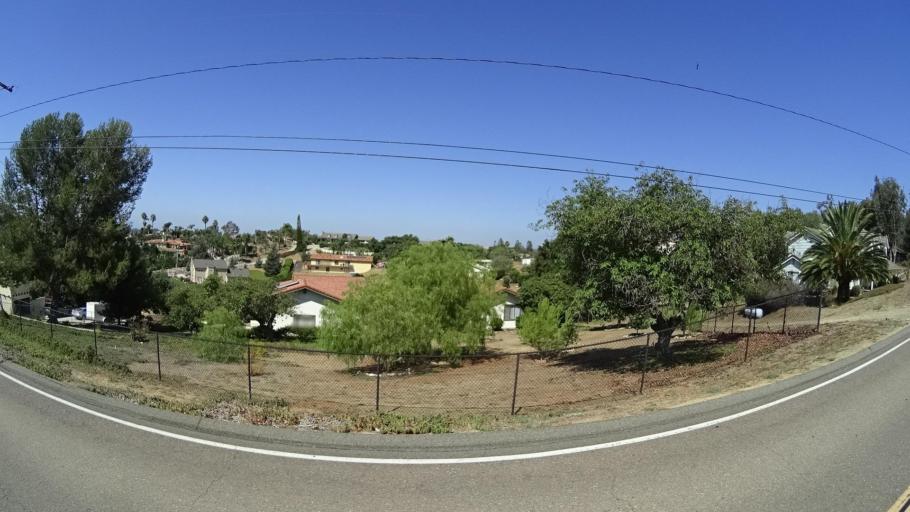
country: US
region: California
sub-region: San Diego County
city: Bonsall
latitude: 33.3203
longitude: -117.2209
